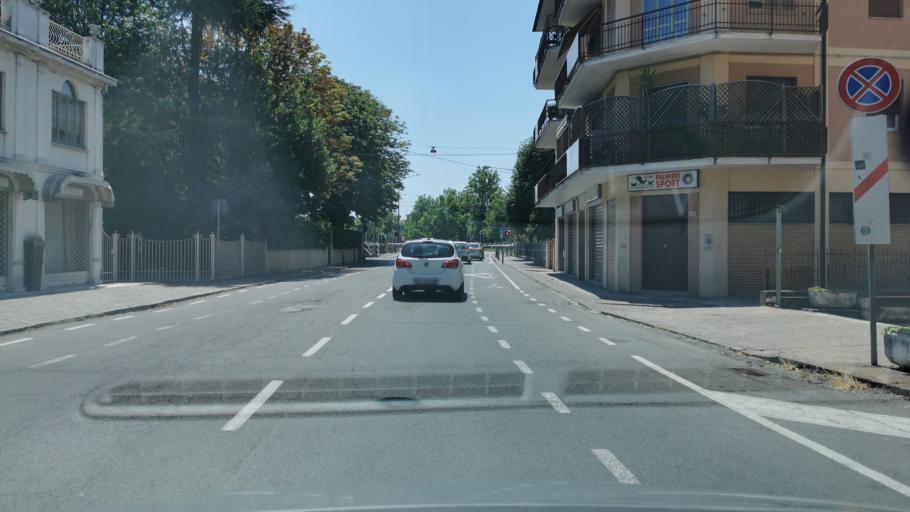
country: IT
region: Emilia-Romagna
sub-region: Provincia di Modena
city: Modena
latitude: 44.6337
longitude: 10.9263
